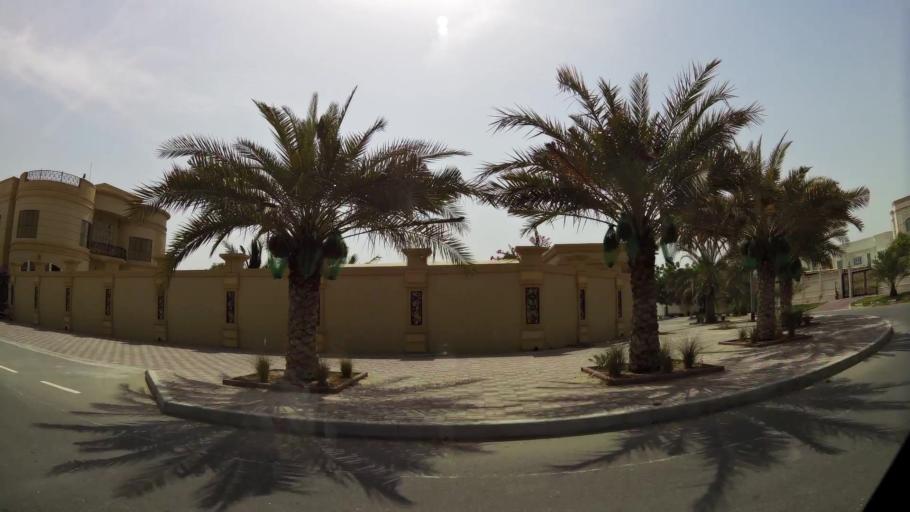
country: AE
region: Ash Shariqah
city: Sharjah
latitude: 25.2350
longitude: 55.4500
